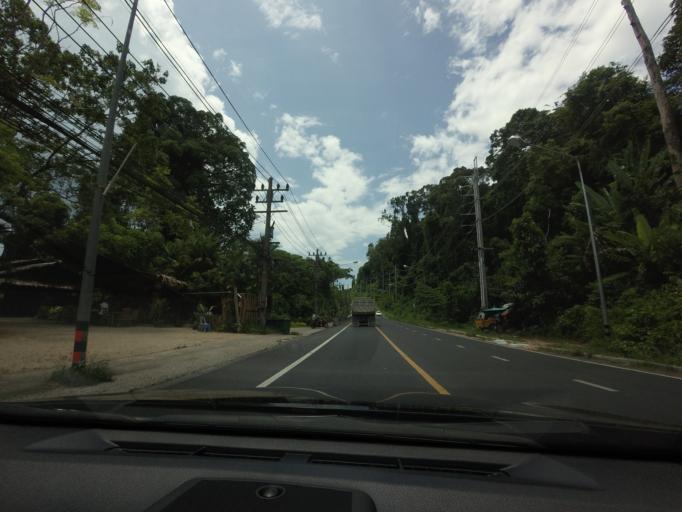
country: TH
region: Phangnga
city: Ban Khao Lak
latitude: 8.6318
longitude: 98.2465
